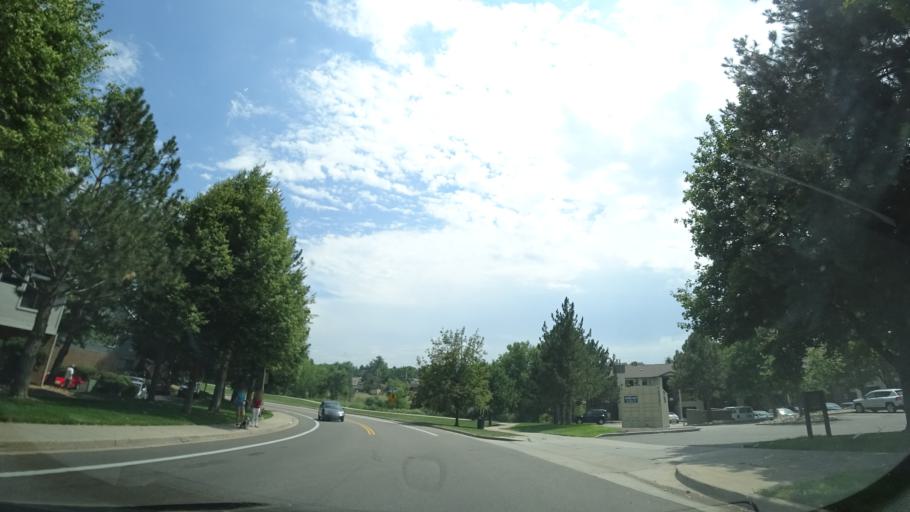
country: US
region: Colorado
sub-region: Jefferson County
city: Lakewood
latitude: 39.7021
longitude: -105.0798
